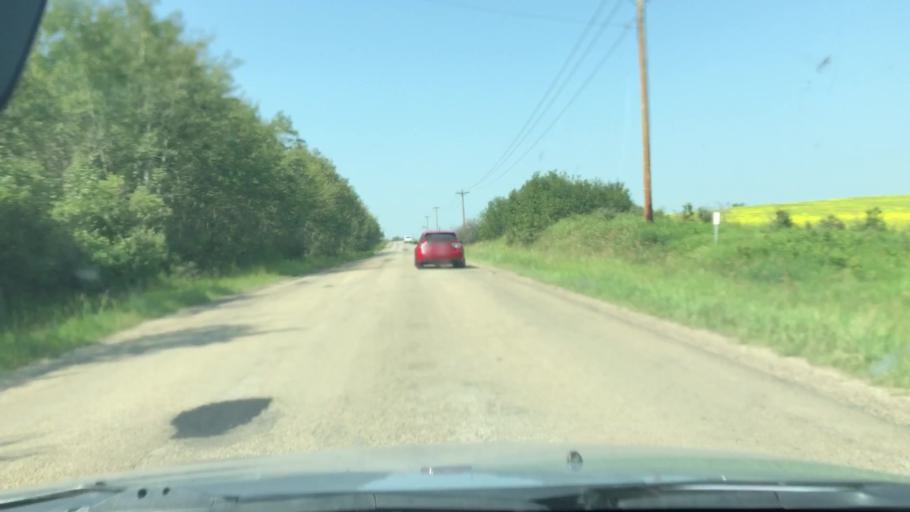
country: CA
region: Alberta
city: Devon
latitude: 53.5122
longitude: -113.7501
